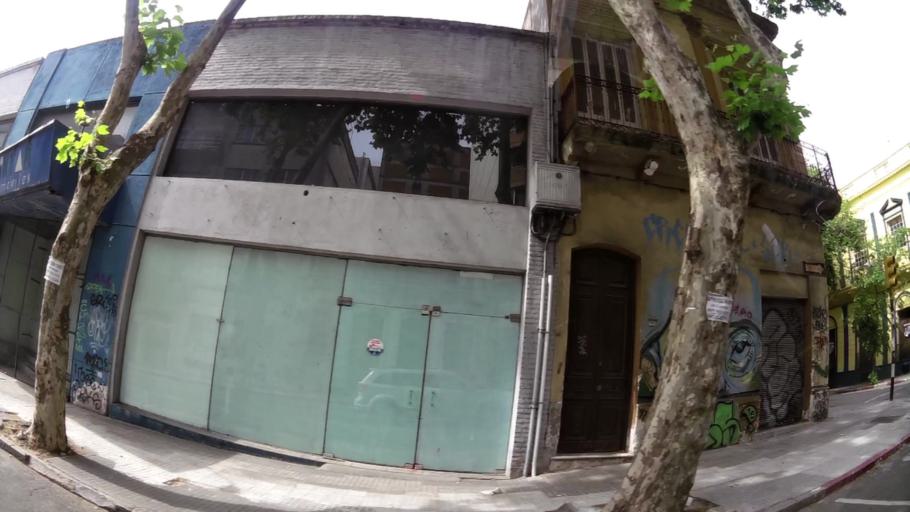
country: UY
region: Montevideo
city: Montevideo
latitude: -34.9083
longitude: -56.1851
